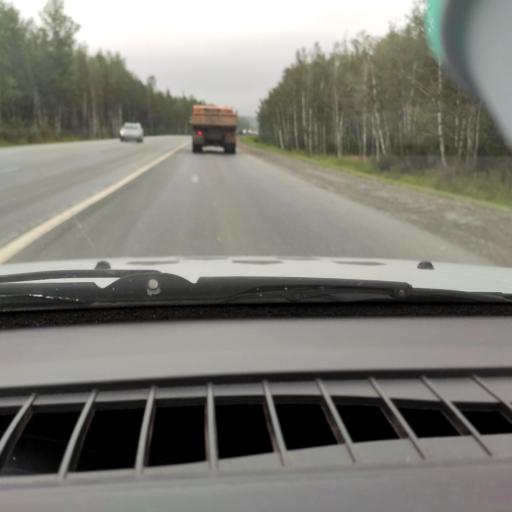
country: RU
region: Chelyabinsk
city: Syrostan
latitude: 55.0183
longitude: 59.7761
